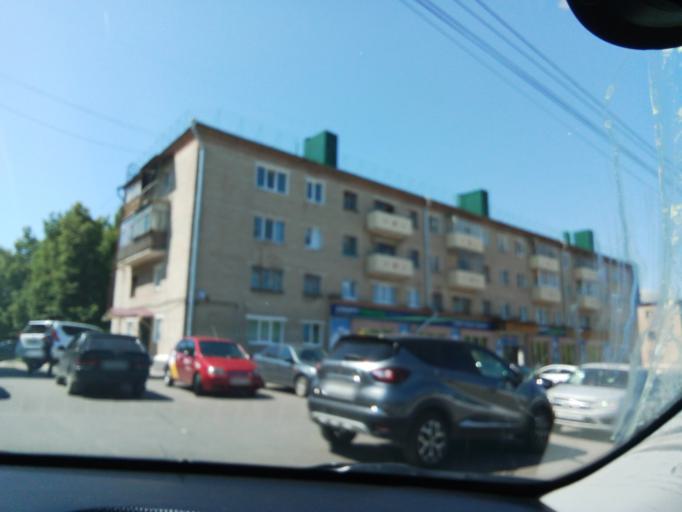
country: RU
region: Chuvashia
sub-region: Cheboksarskiy Rayon
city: Cheboksary
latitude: 56.1216
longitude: 47.2646
